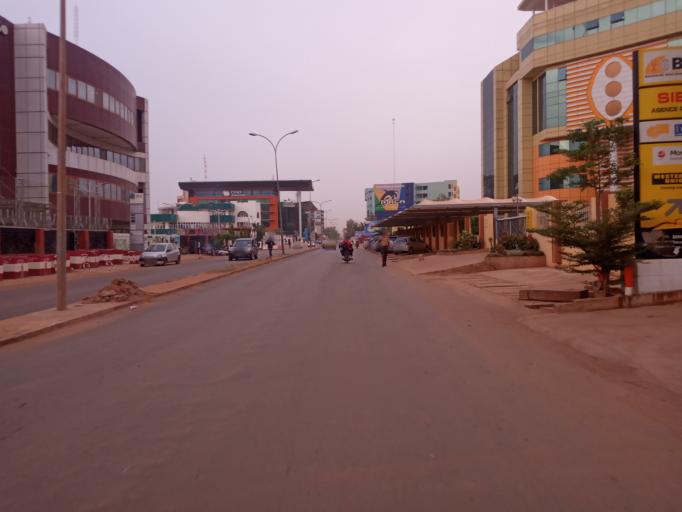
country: ML
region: Bamako
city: Bamako
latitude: 12.6346
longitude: -8.0258
